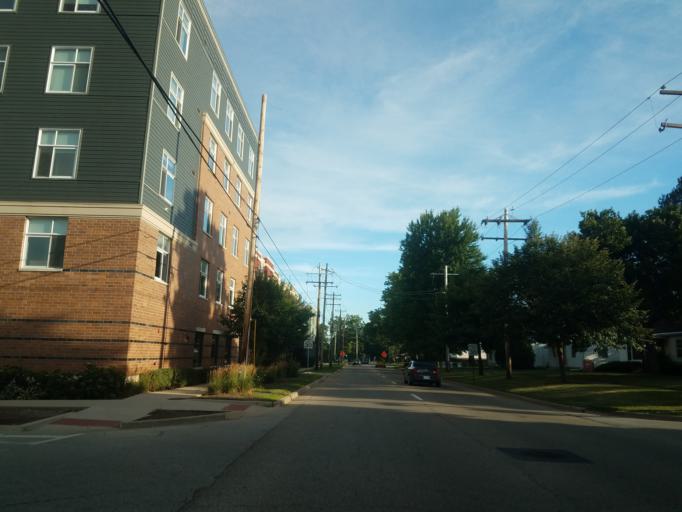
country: US
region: Illinois
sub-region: McLean County
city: Normal
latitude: 40.5045
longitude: -88.9965
